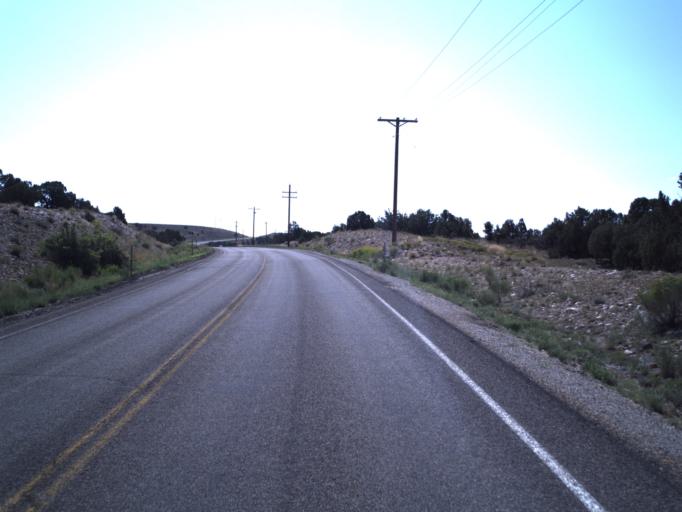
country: US
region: Utah
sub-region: Duchesne County
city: Duchesne
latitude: 40.2555
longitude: -110.4048
